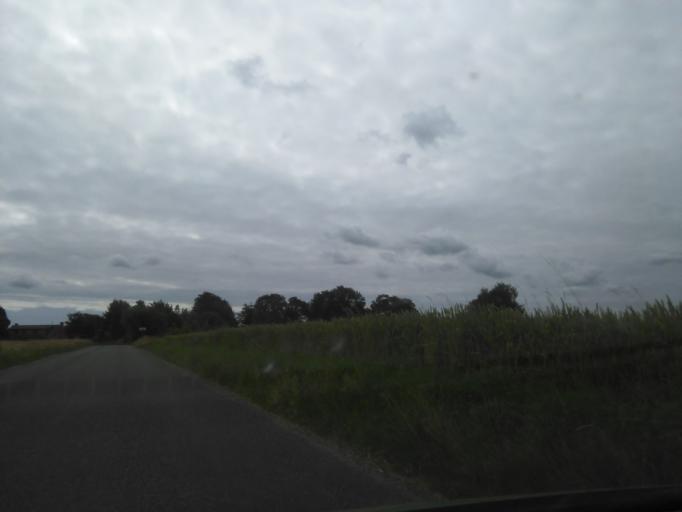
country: DK
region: Central Jutland
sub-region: Arhus Kommune
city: Solbjerg
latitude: 56.0225
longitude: 10.0724
